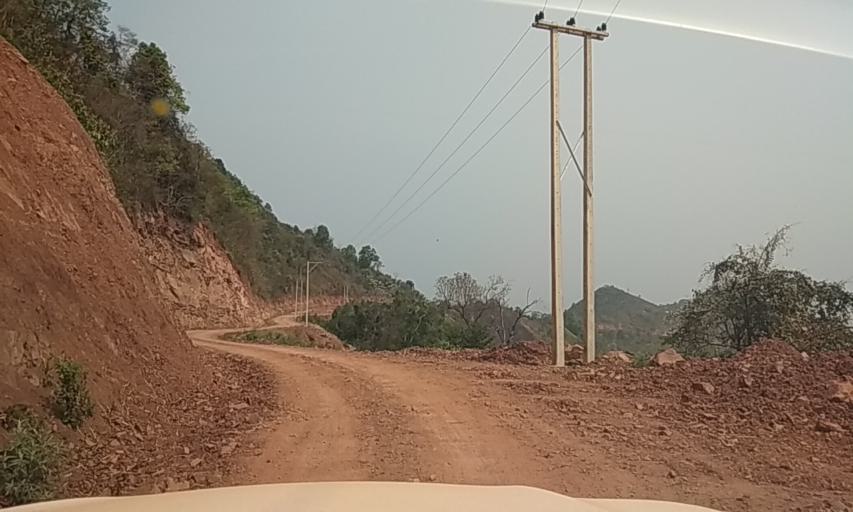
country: VN
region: Huyen Dien Bien
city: Dien Bien Phu
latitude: 21.5005
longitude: 102.7917
